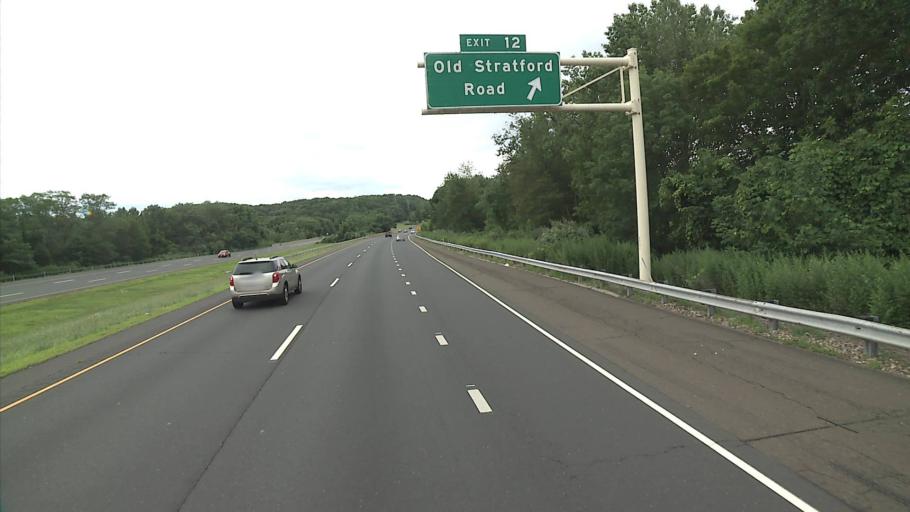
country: US
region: Connecticut
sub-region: Fairfield County
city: Shelton
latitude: 41.2783
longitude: -73.1141
